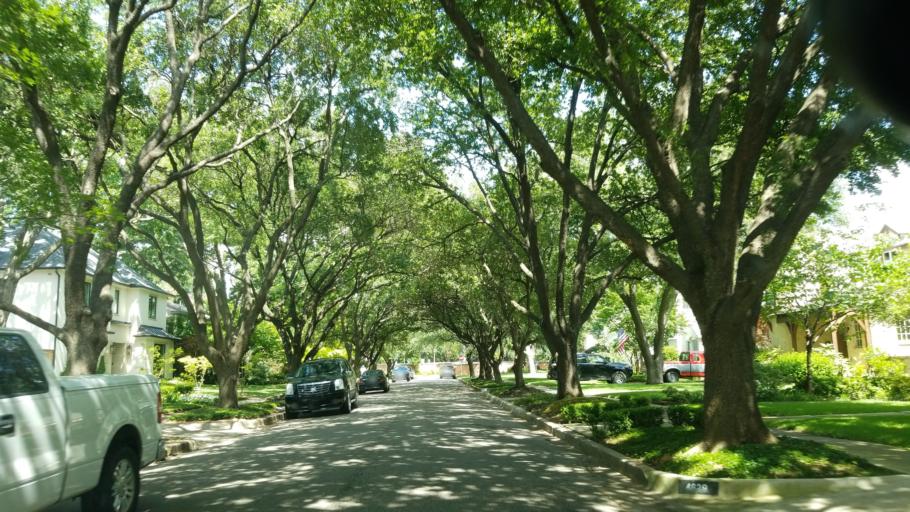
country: US
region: Texas
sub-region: Dallas County
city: Highland Park
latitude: 32.8286
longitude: -96.8174
